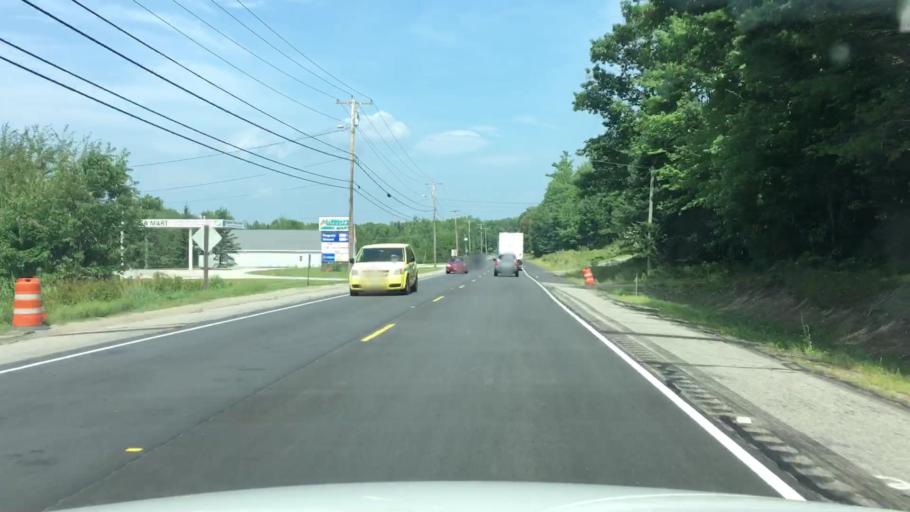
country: US
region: Maine
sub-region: Androscoggin County
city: Turner
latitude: 44.2125
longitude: -70.2460
